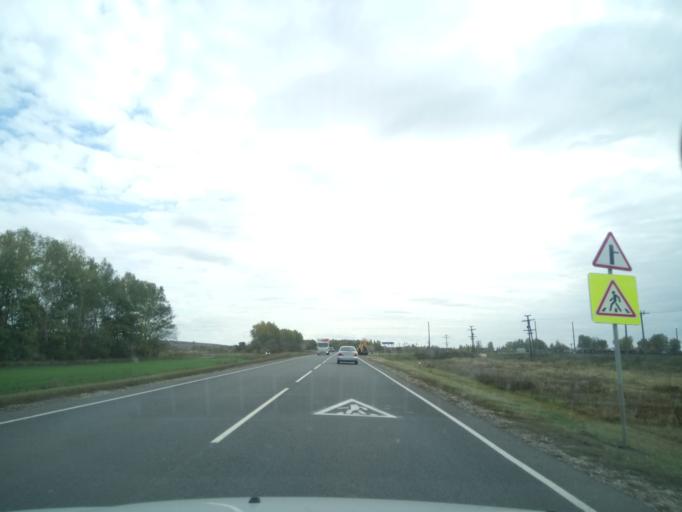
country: RU
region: Nizjnij Novgorod
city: Lukoyanov
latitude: 55.0692
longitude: 44.3436
